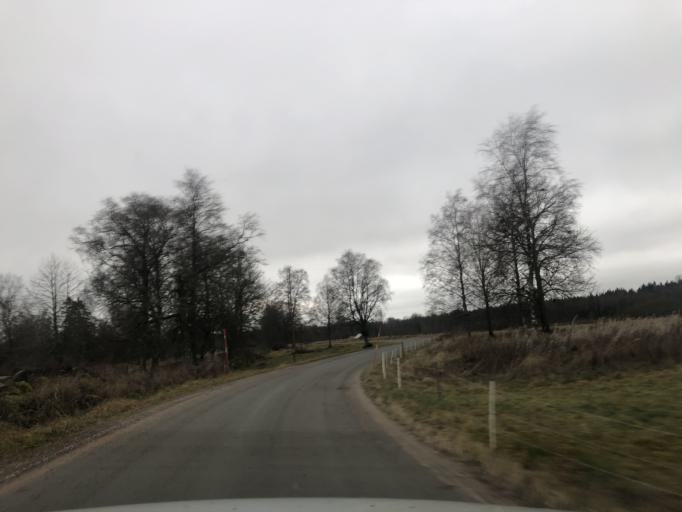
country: SE
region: Vaestra Goetaland
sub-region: Ulricehamns Kommun
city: Ulricehamn
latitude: 57.8878
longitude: 13.4169
